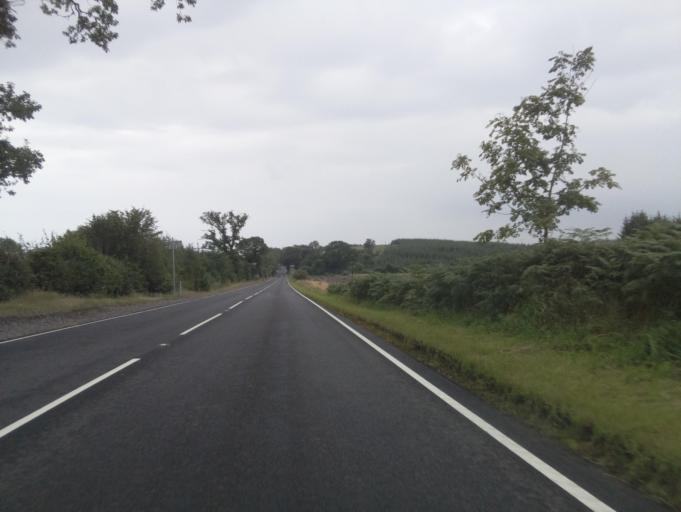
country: GB
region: Scotland
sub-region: Dumfries and Galloway
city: Moffat
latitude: 55.2636
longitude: -3.4547
